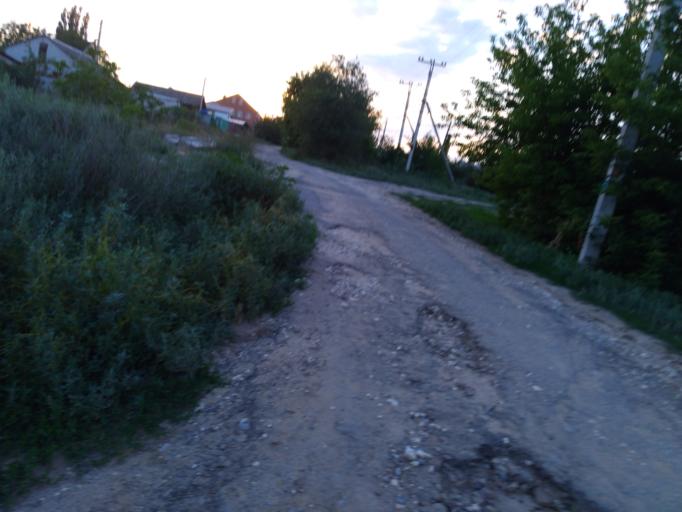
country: RU
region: Volgograd
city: Volgograd
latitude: 48.6690
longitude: 44.4538
